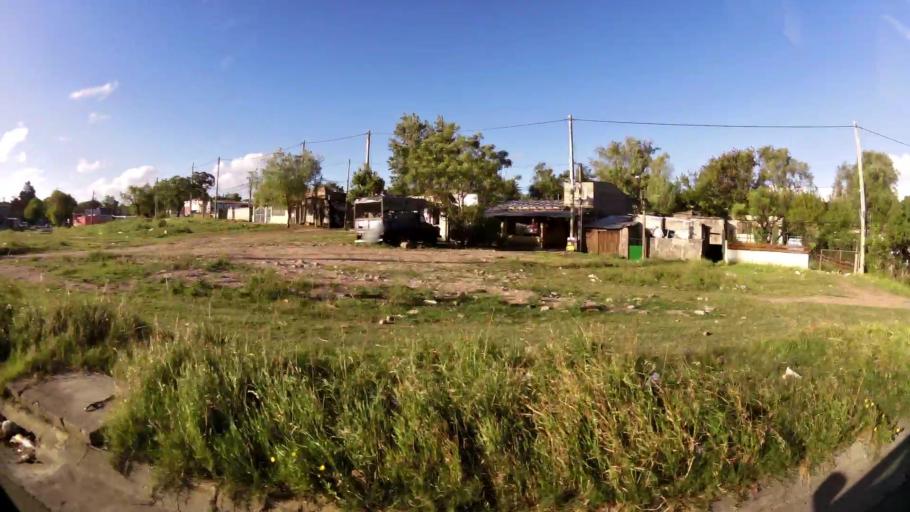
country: UY
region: Montevideo
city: Montevideo
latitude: -34.8794
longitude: -56.1323
